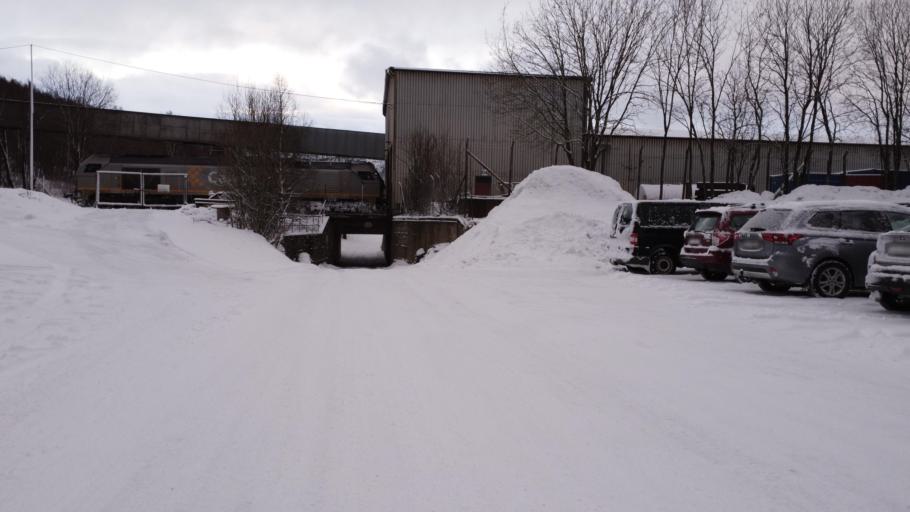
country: NO
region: Nordland
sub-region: Rana
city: Mo i Rana
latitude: 66.3263
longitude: 14.1522
